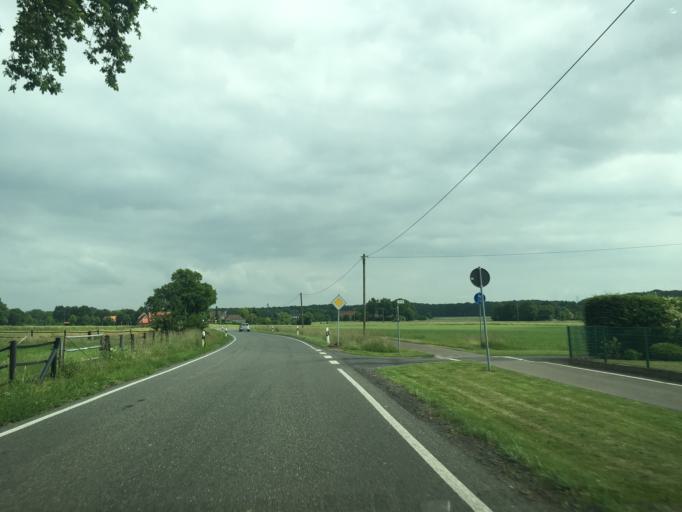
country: DE
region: North Rhine-Westphalia
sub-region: Regierungsbezirk Munster
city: Horstmar
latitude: 52.1002
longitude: 7.3198
